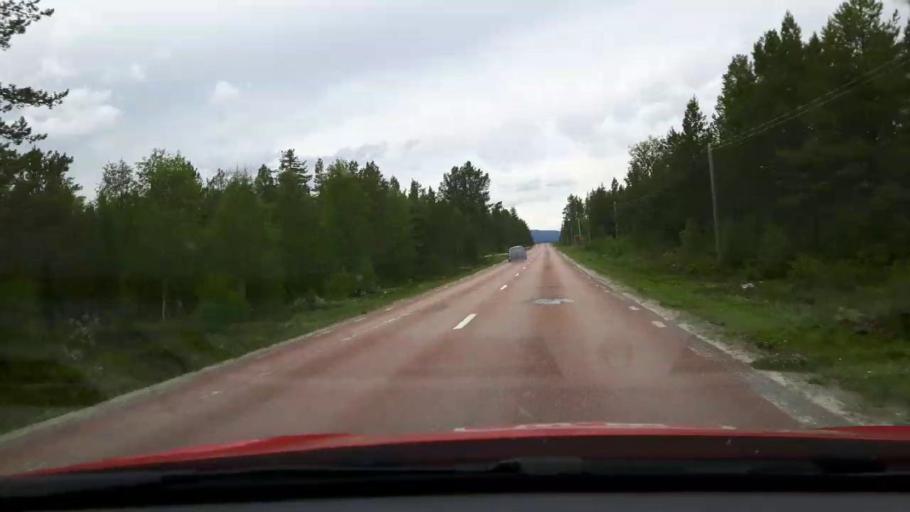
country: NO
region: Hedmark
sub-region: Engerdal
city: Engerdal
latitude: 62.4958
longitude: 12.6339
